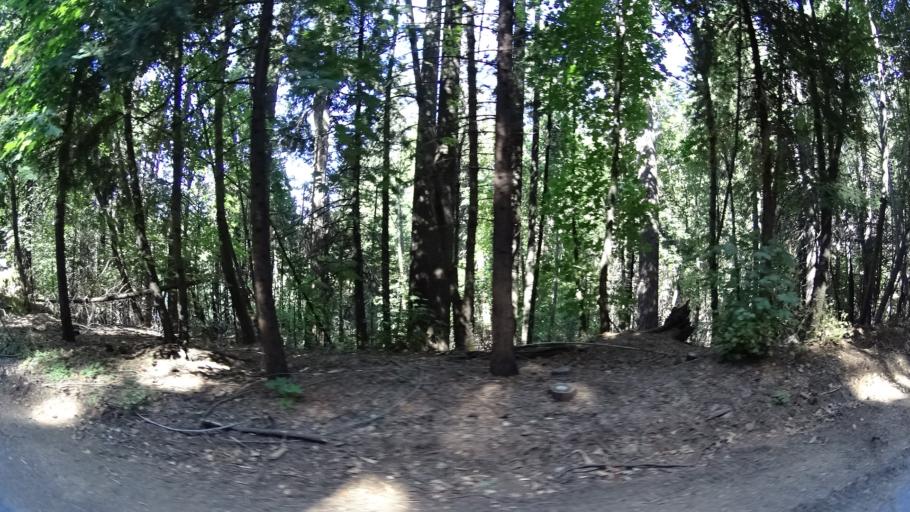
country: US
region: California
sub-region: Calaveras County
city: Arnold
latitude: 38.2589
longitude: -120.3234
